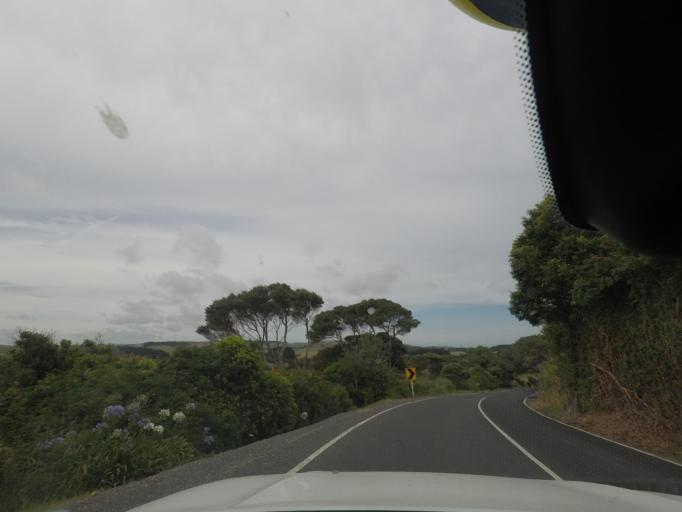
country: NZ
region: Auckland
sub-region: Auckland
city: Parakai
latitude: -36.5105
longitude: 174.2477
